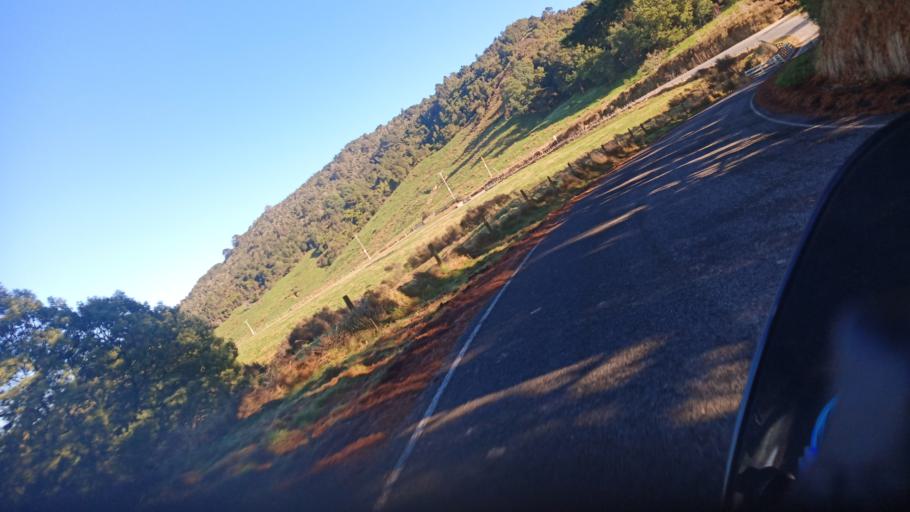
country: NZ
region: Gisborne
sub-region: Gisborne District
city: Gisborne
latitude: -38.5878
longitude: 177.5374
